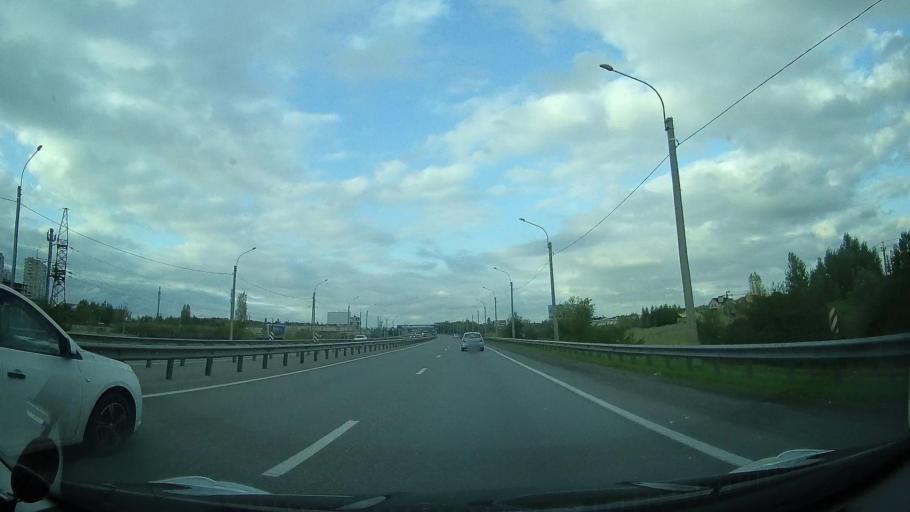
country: RU
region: Rostov
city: Bataysk
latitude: 47.1343
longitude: 39.7761
